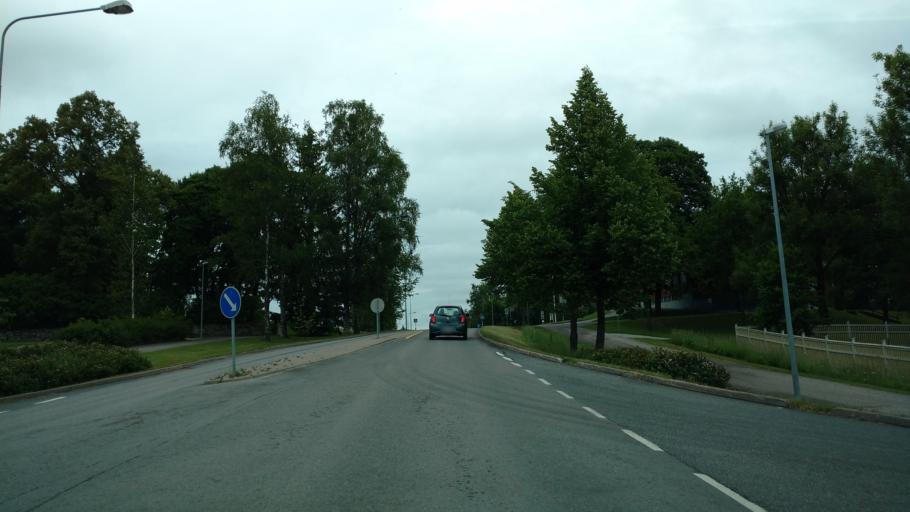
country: FI
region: Varsinais-Suomi
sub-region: Salo
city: Halikko
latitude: 60.3999
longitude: 23.0746
